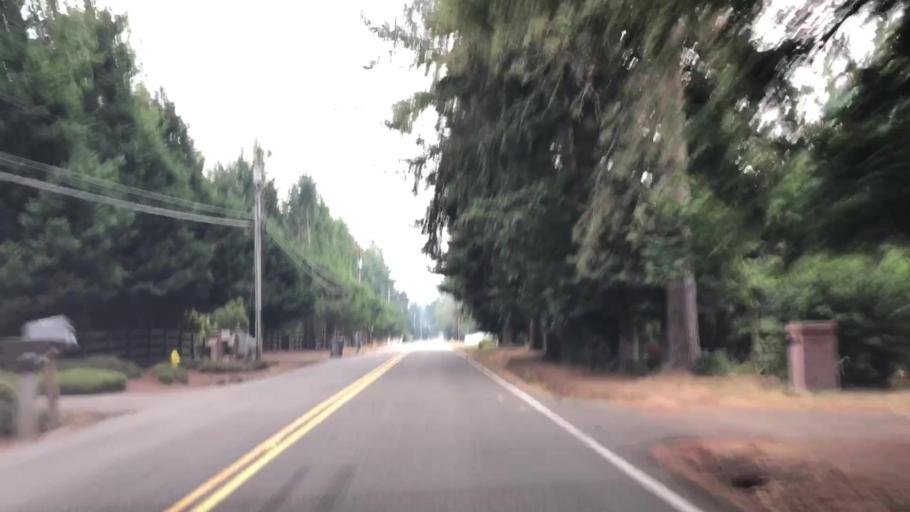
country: US
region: Washington
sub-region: King County
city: Cottage Lake
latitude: 47.7344
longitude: -122.1153
